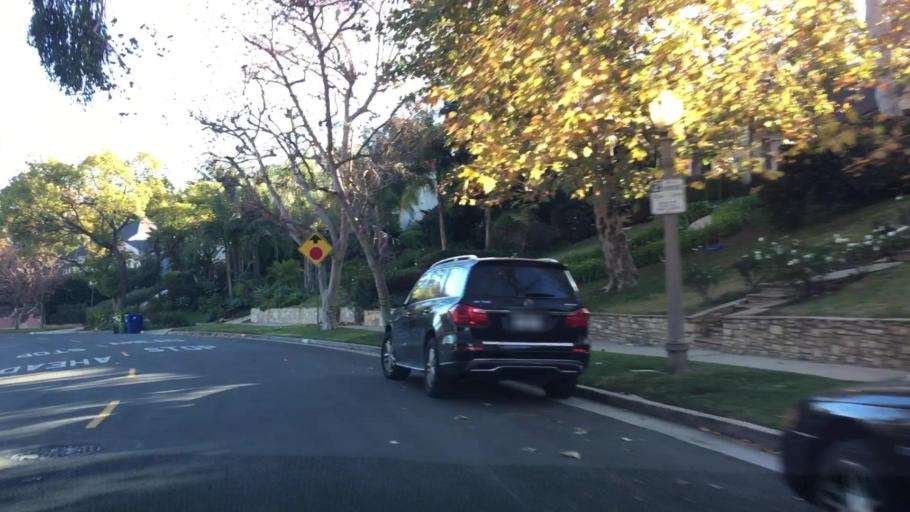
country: US
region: California
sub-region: Los Angeles County
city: Westwood, Los Angeles
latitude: 34.0655
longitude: -118.4252
